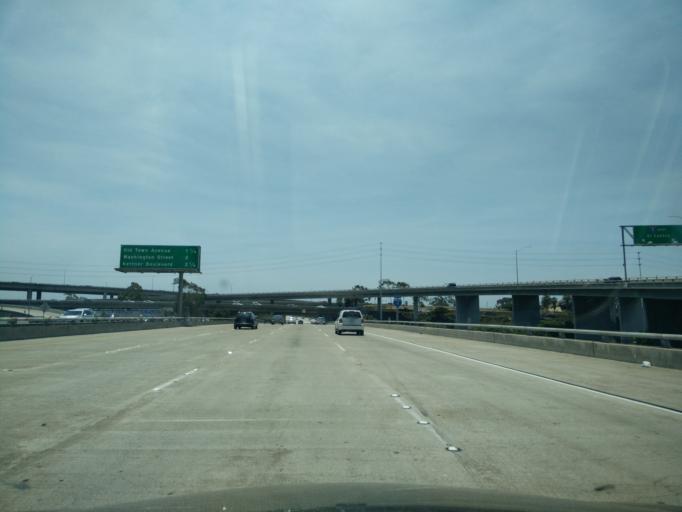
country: US
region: California
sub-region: San Diego County
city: San Diego
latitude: 32.7617
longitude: -117.2047
